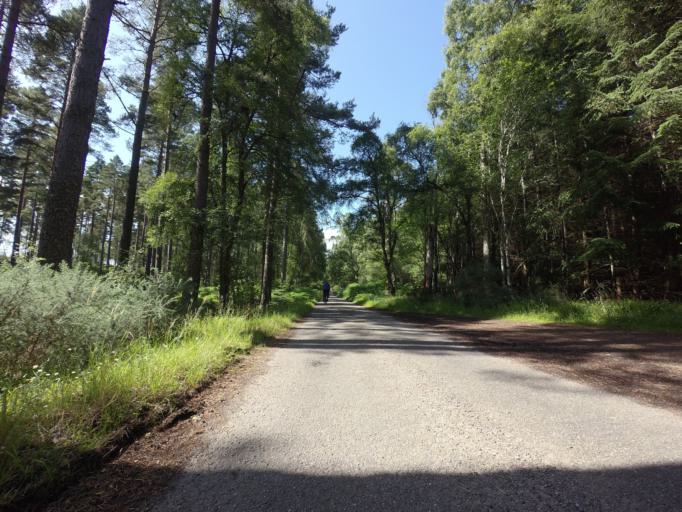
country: GB
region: Scotland
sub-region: Highland
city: Nairn
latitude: 57.5070
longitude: -3.9057
